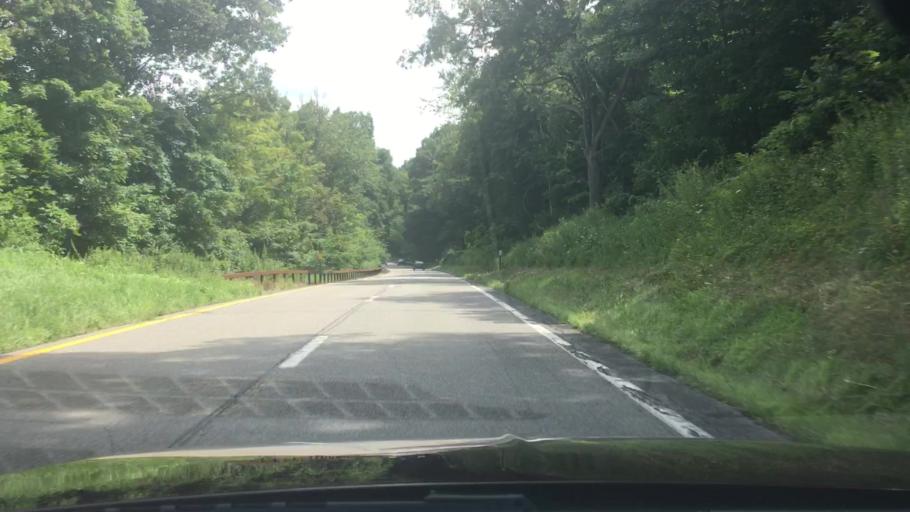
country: US
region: New York
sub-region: Dutchess County
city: Hillside Lake
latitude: 41.6204
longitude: -73.7671
